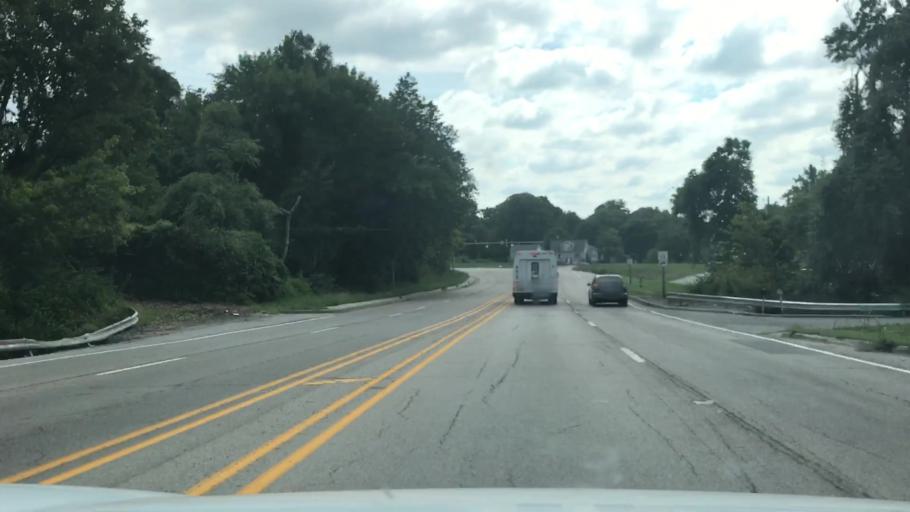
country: US
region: Illinois
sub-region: Saint Clair County
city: Swansea
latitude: 38.5435
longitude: -90.0494
